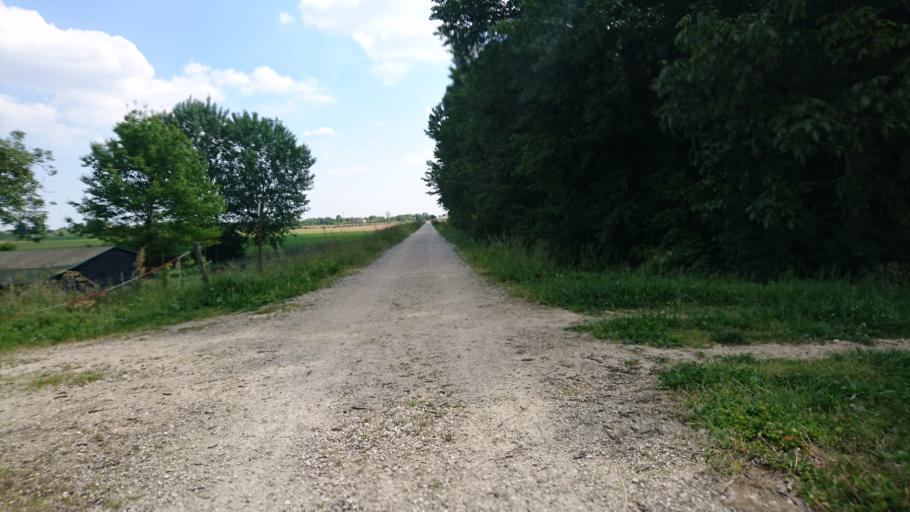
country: IT
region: Veneto
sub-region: Provincia di Padova
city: Veggiano
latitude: 45.4404
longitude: 11.7254
